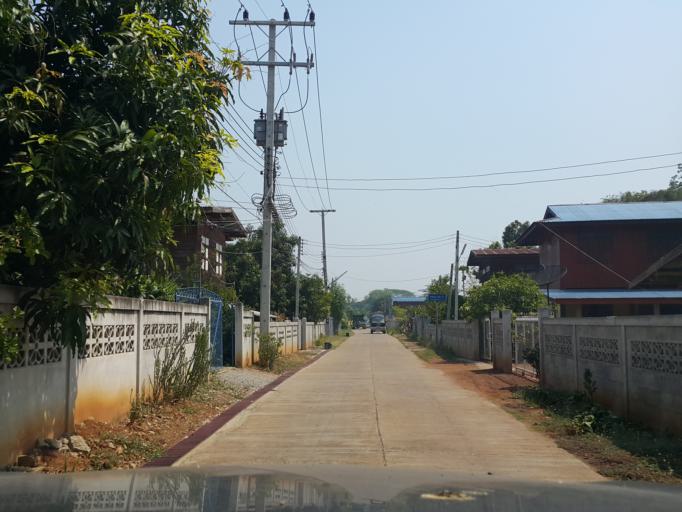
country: TH
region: Sukhothai
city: Thung Saliam
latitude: 17.3133
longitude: 99.5456
